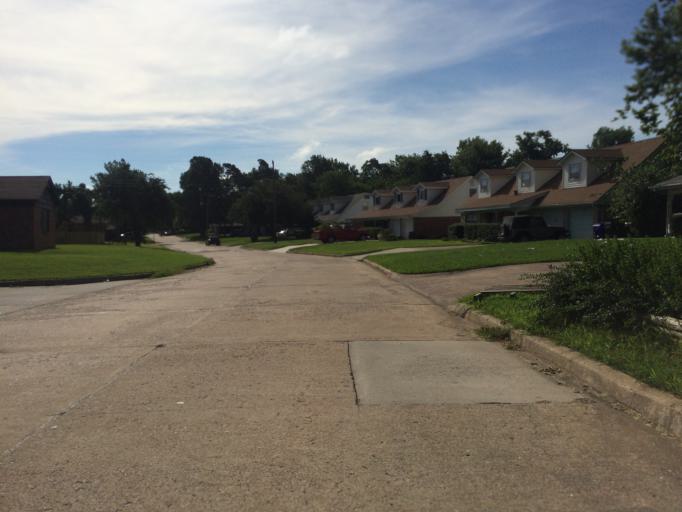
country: US
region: Oklahoma
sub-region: Cleveland County
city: Norman
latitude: 35.2212
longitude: -97.4742
